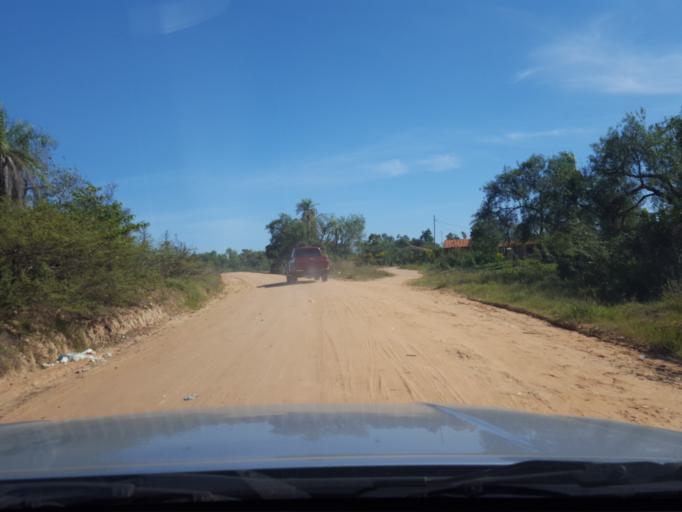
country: PY
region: Cordillera
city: Tobati
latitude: -25.2542
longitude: -57.1033
